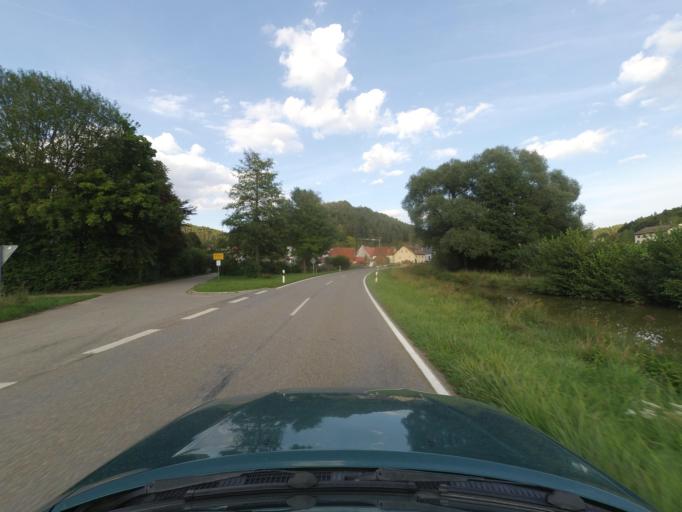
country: DE
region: Bavaria
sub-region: Upper Palatinate
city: Hirschbach
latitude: 49.5669
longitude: 11.5626
